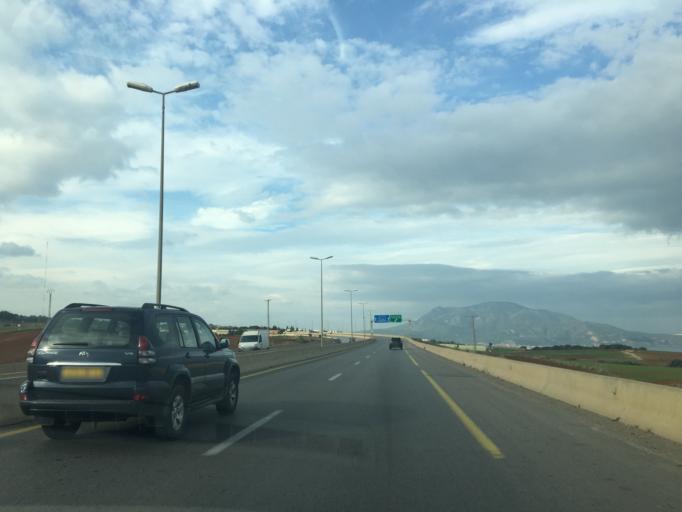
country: DZ
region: Tipaza
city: Tipasa
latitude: 36.5768
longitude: 2.5074
